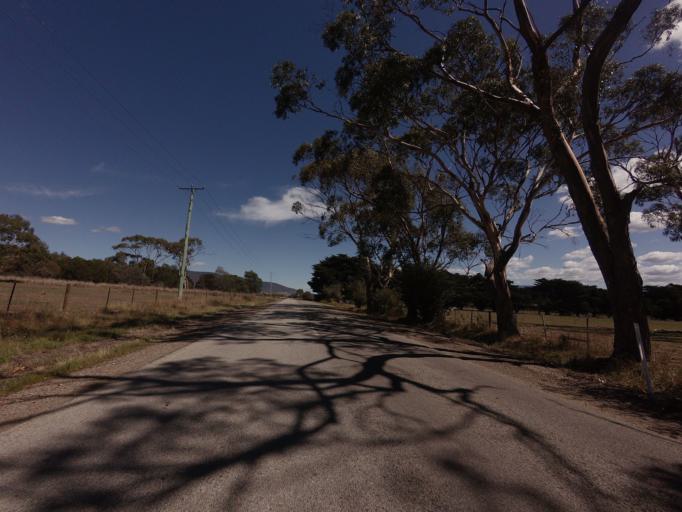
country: AU
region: Tasmania
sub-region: Break O'Day
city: St Helens
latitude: -41.6172
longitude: 148.0077
